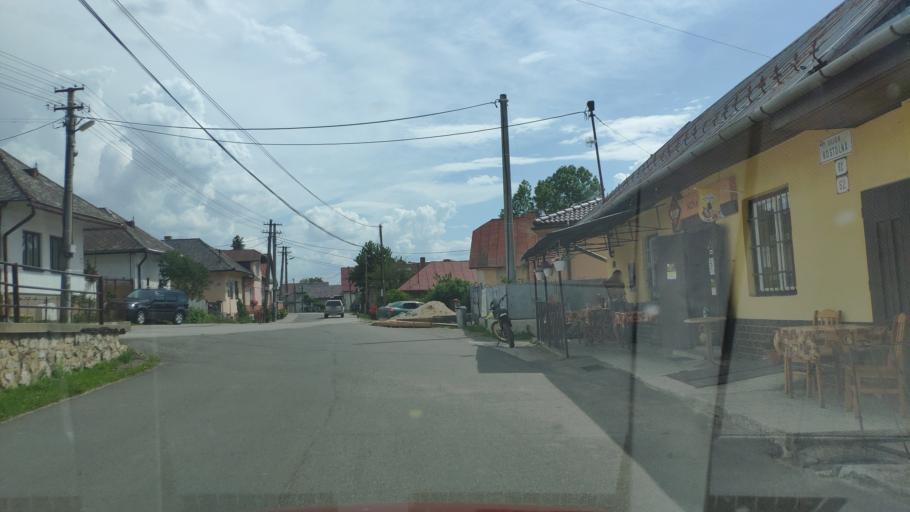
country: SK
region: Kosicky
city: Medzev
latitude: 48.7084
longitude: 20.9748
